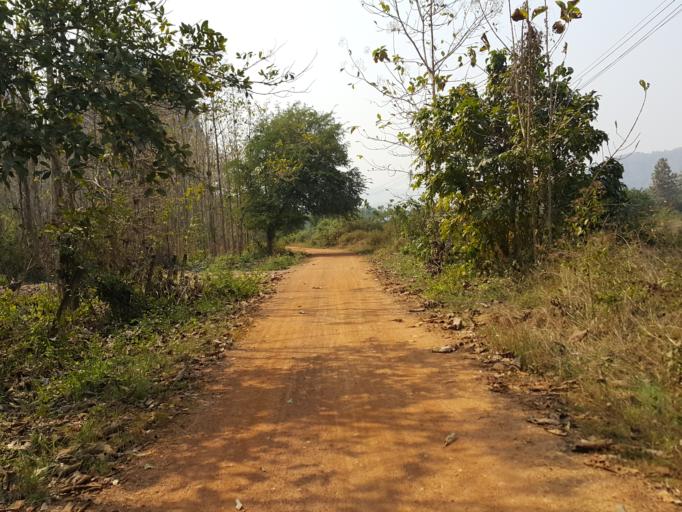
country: TH
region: Sukhothai
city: Thung Saliam
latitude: 17.3100
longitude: 99.5094
